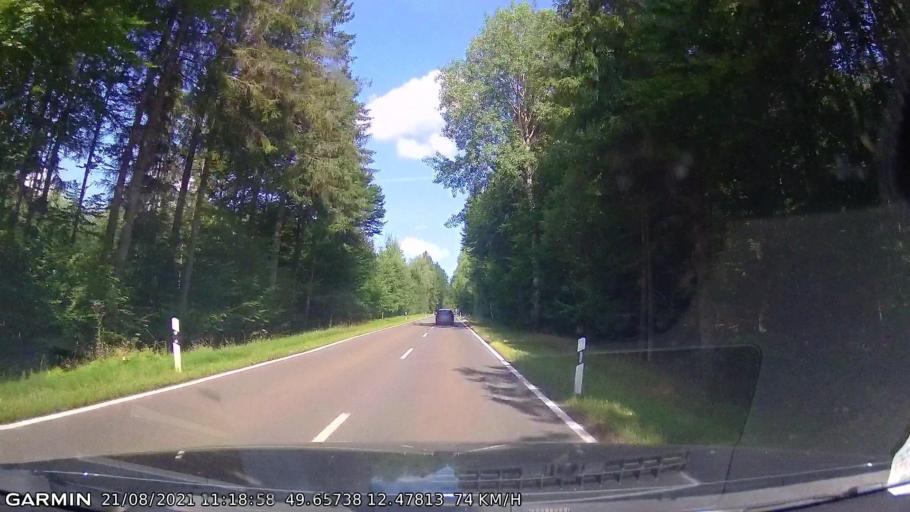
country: DE
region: Bavaria
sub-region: Upper Palatinate
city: Waidhaus
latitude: 49.6574
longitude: 12.4781
